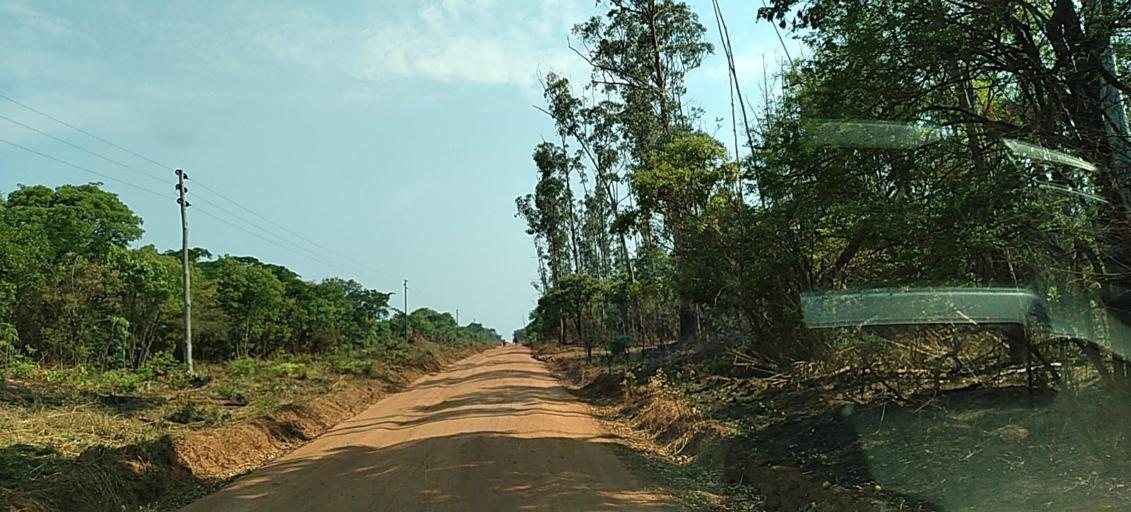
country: ZM
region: Copperbelt
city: Kalulushi
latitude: -12.9985
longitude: 27.8139
